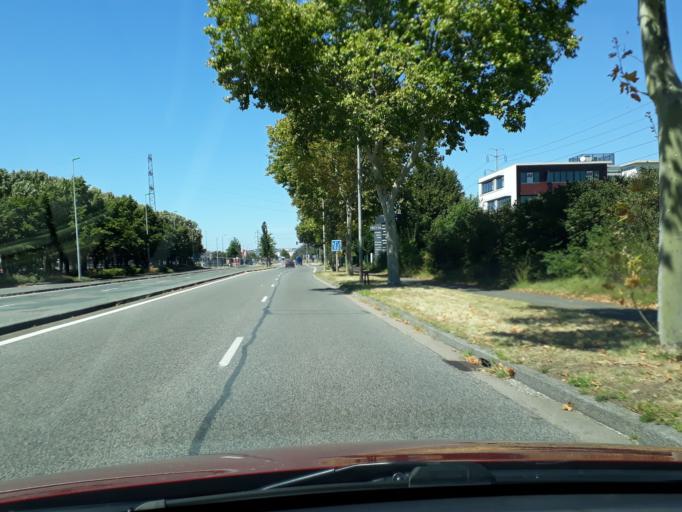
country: FR
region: Rhone-Alpes
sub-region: Departement du Rhone
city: Bron
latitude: 45.7097
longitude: 4.9045
